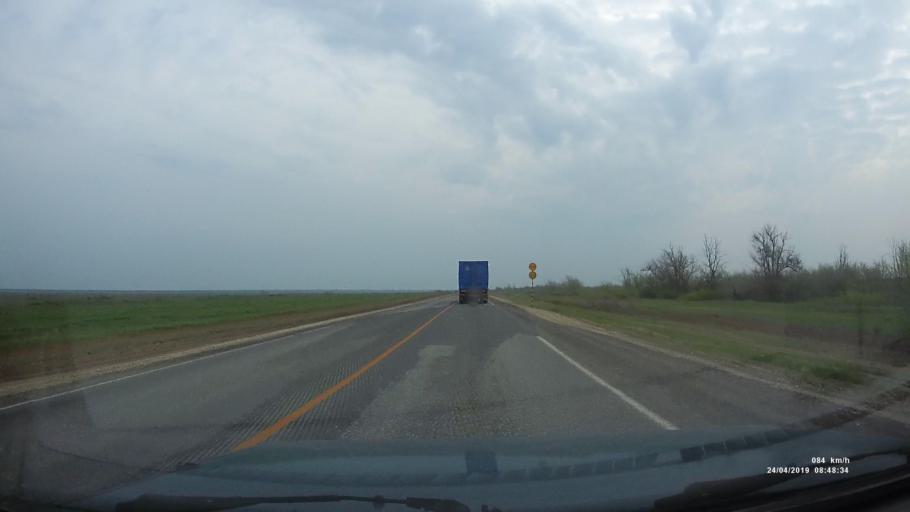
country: RU
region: Kalmykiya
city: Arshan'
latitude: 46.2518
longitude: 44.1110
